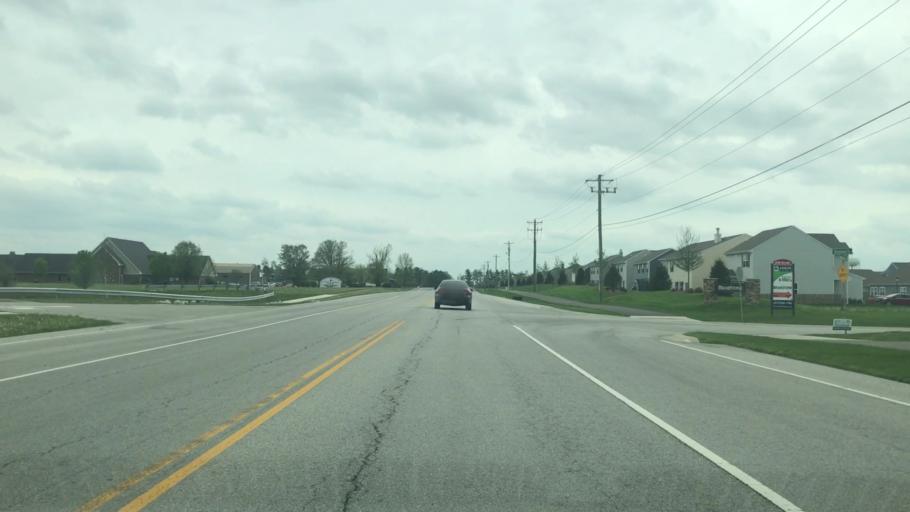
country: US
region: Indiana
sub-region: Johnson County
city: New Whiteland
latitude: 39.5860
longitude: -86.0830
